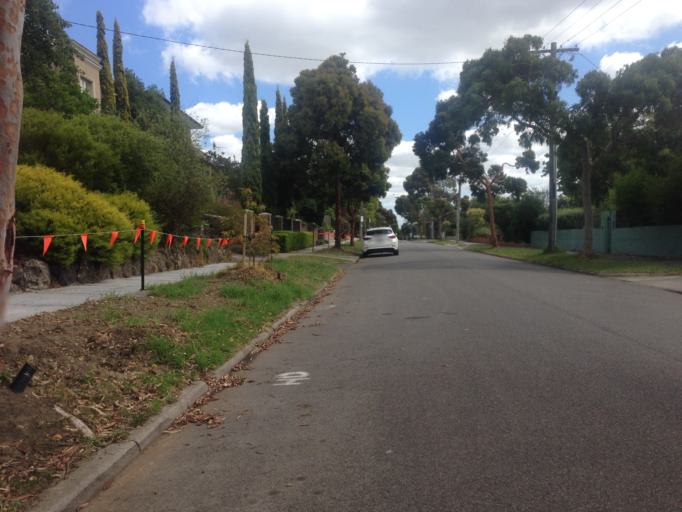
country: AU
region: Victoria
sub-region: Boroondara
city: Balwyn North
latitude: -37.7881
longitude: 145.0826
